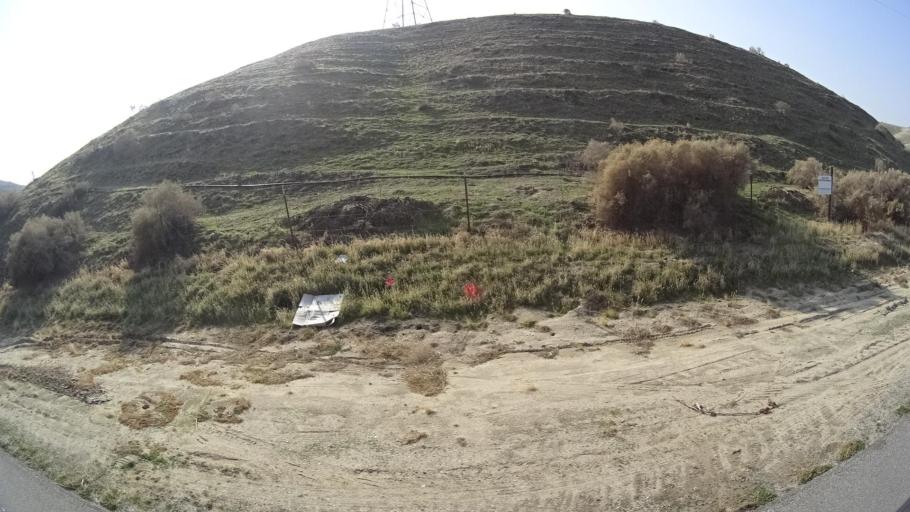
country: US
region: California
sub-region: Kern County
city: Buttonwillow
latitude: 35.2846
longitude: -119.3317
